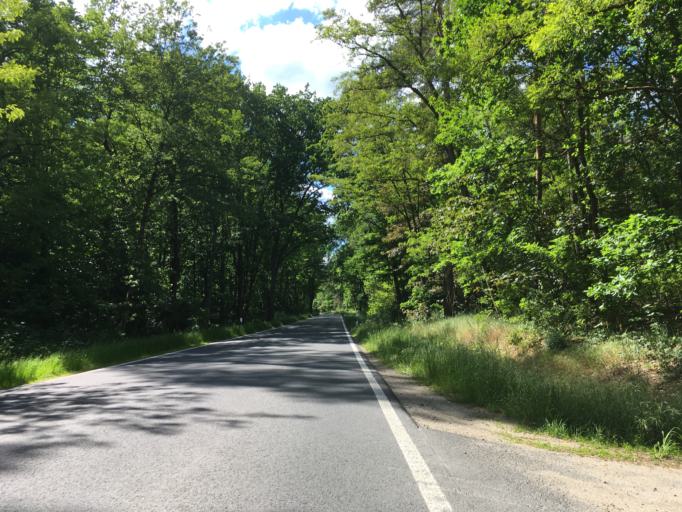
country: DE
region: Brandenburg
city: Protzel
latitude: 52.6012
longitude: 13.9936
